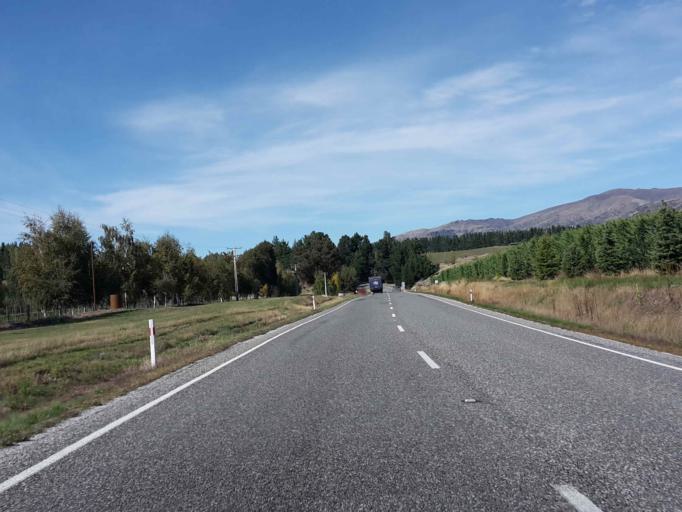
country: NZ
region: Otago
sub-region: Queenstown-Lakes District
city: Wanaka
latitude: -44.7016
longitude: 169.1936
